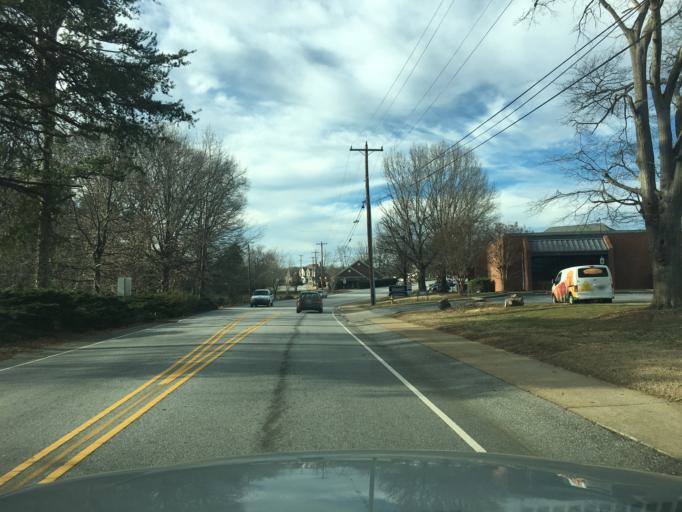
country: US
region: South Carolina
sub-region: Greenville County
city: Greer
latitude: 34.9402
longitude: -82.2471
